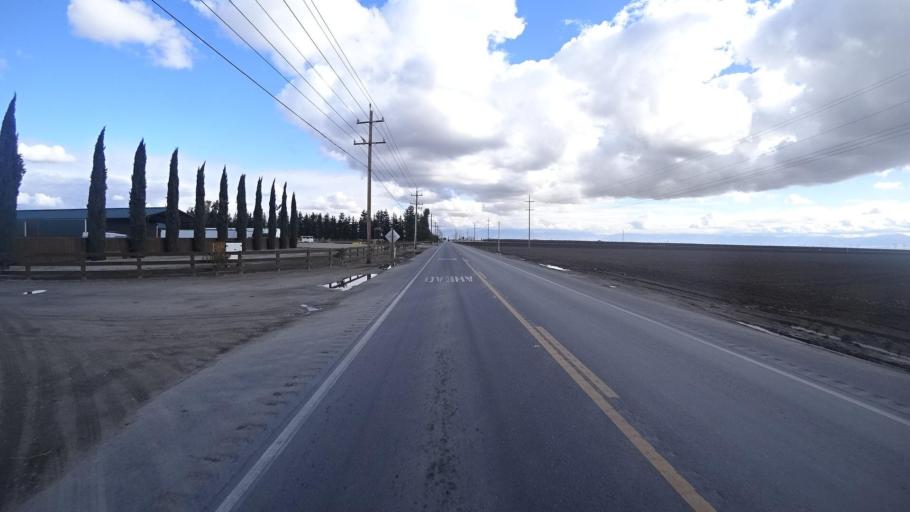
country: US
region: California
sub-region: Kern County
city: Greenfield
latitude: 35.2089
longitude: -119.1086
